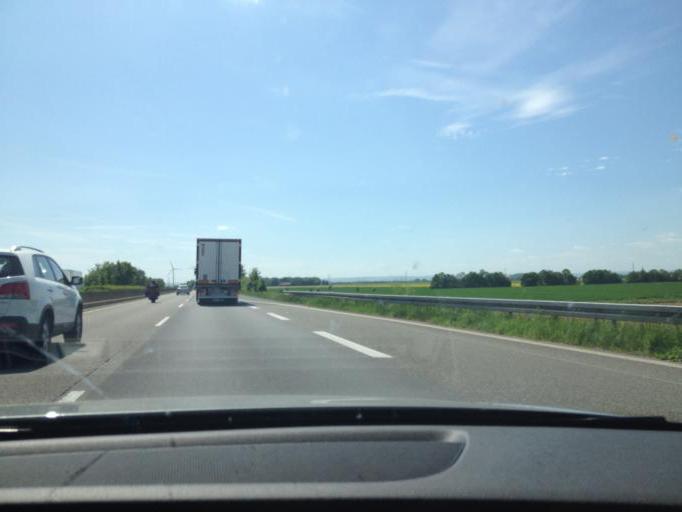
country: DE
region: North Rhine-Westphalia
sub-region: Regierungsbezirk Koln
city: Weilerswist
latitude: 50.7392
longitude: 6.7972
